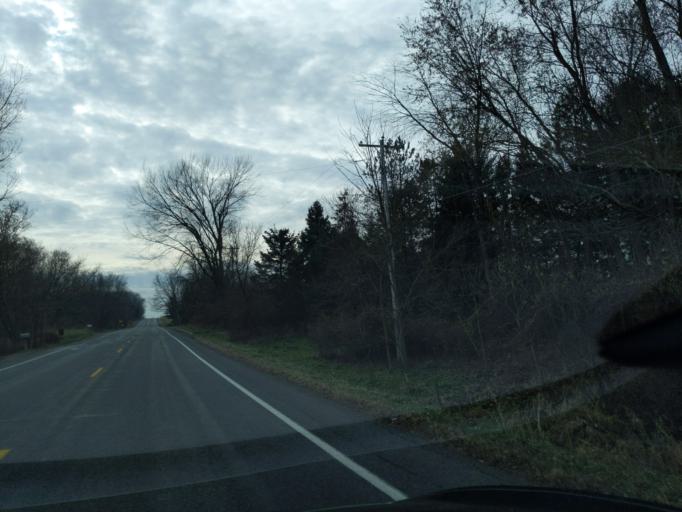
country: US
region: Michigan
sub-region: Ingham County
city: Holt
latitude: 42.6038
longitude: -84.5231
